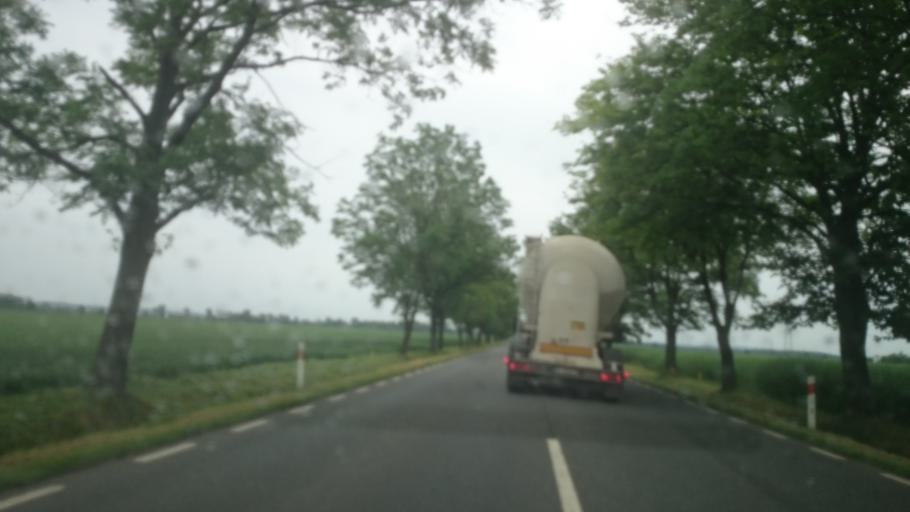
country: PL
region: Opole Voivodeship
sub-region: Powiat nyski
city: Paczkow
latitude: 50.4510
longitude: 17.0708
